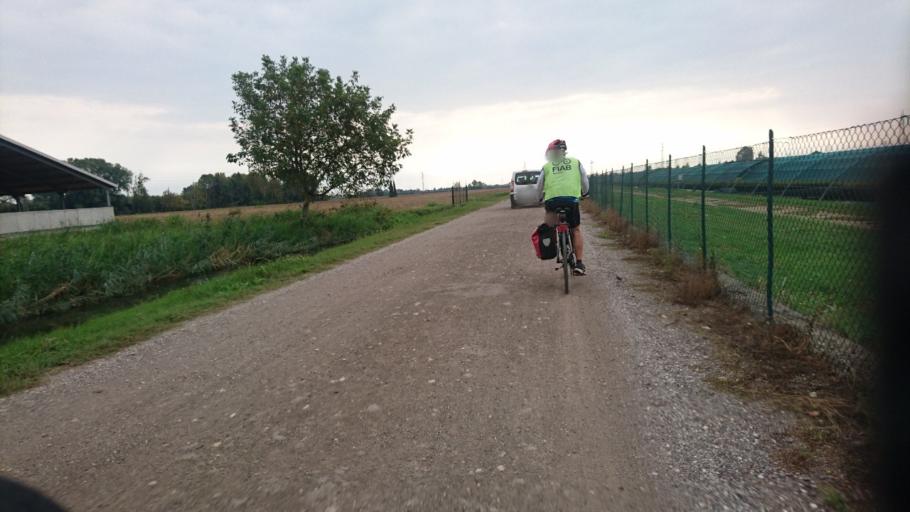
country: IT
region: Veneto
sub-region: Provincia di Verona
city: San Martino Buon Albergo
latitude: 45.4047
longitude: 11.1089
